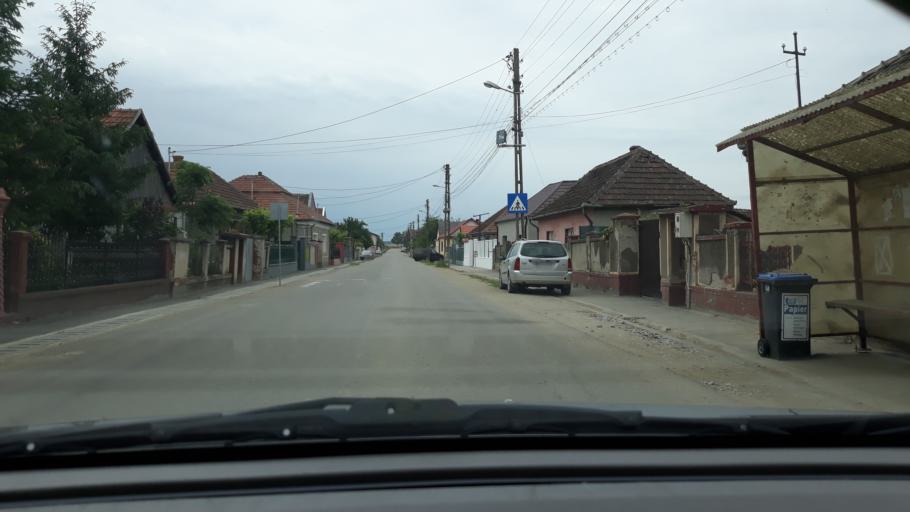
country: RO
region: Bihor
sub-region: Comuna Osorheiu
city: Osorheiu
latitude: 47.0567
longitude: 22.0444
